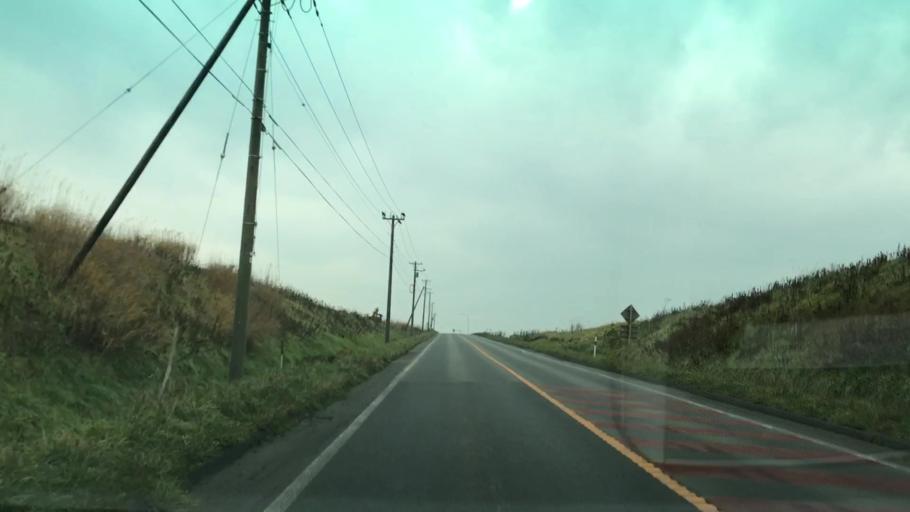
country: JP
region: Hokkaido
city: Ishikari
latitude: 43.3526
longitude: 141.4272
